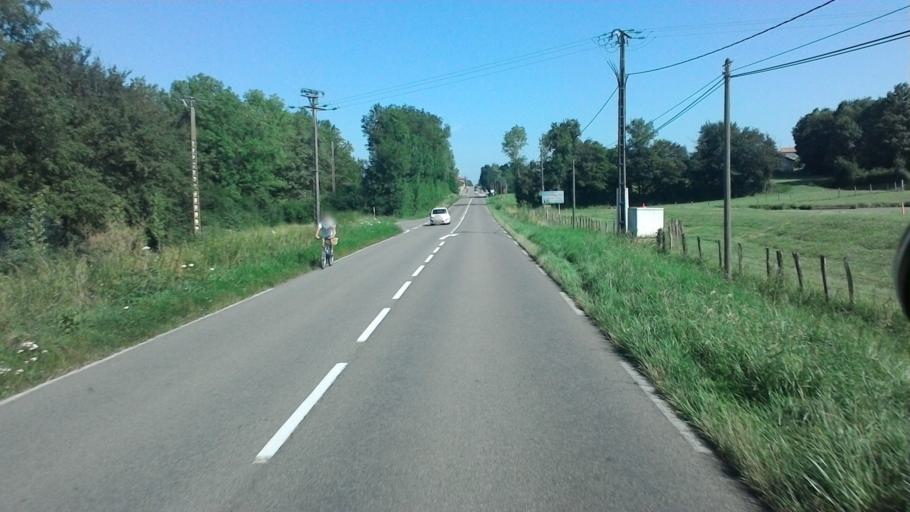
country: FR
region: Rhone-Alpes
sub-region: Departement de l'Ain
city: Saint-Trivier-de-Courtes
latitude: 46.4194
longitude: 5.1012
